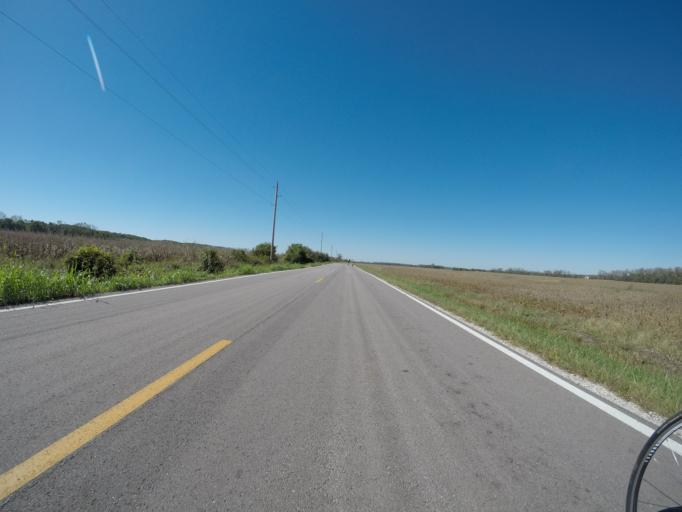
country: US
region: Kansas
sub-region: Johnson County
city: De Soto
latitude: 38.9857
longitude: -94.9833
